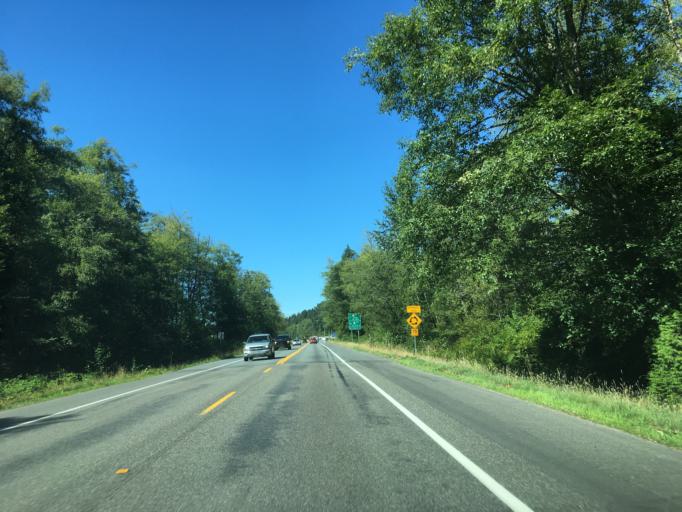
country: US
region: Washington
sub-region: Snohomish County
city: Sisco Heights
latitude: 48.1469
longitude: -122.1131
